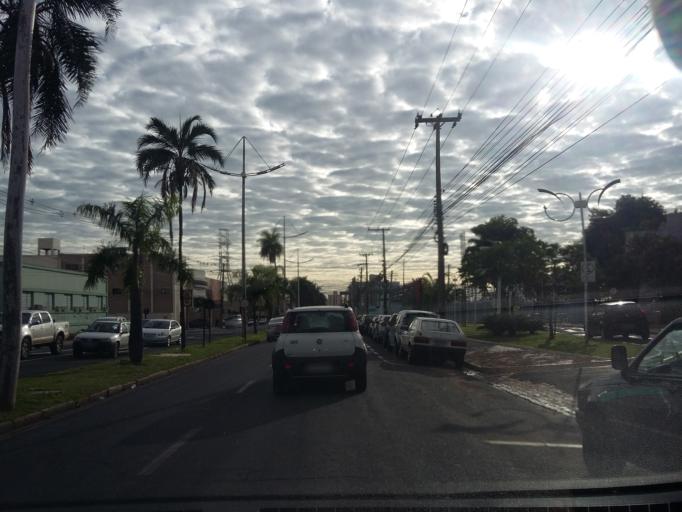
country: BR
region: Sao Paulo
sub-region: Sao Jose Do Rio Preto
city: Sao Jose do Rio Preto
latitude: -20.8281
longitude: -49.3962
